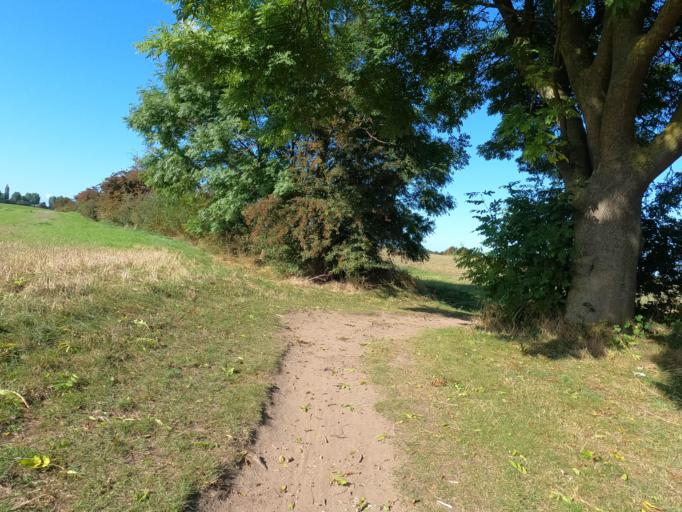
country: DE
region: Schleswig-Holstein
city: Grossenbrode
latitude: 54.3486
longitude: 11.0602
